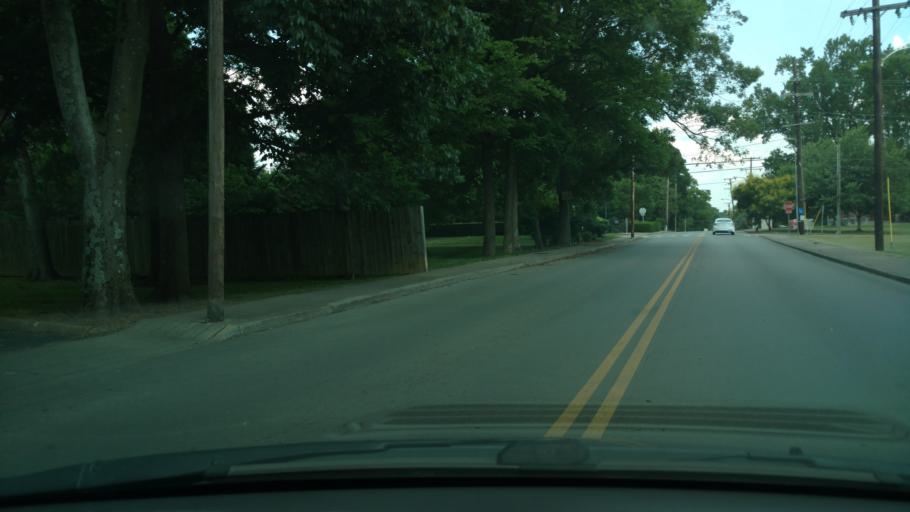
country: US
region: Tennessee
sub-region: Davidson County
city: Nashville
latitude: 36.1892
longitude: -86.7344
